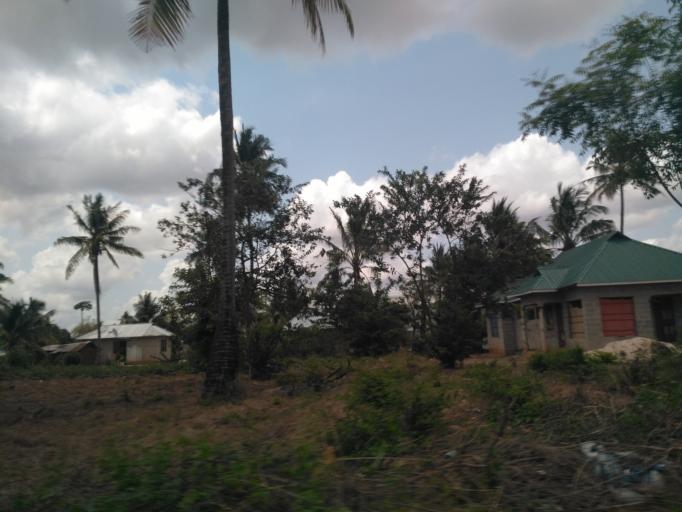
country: TZ
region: Dar es Salaam
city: Dar es Salaam
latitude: -6.8624
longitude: 39.3508
